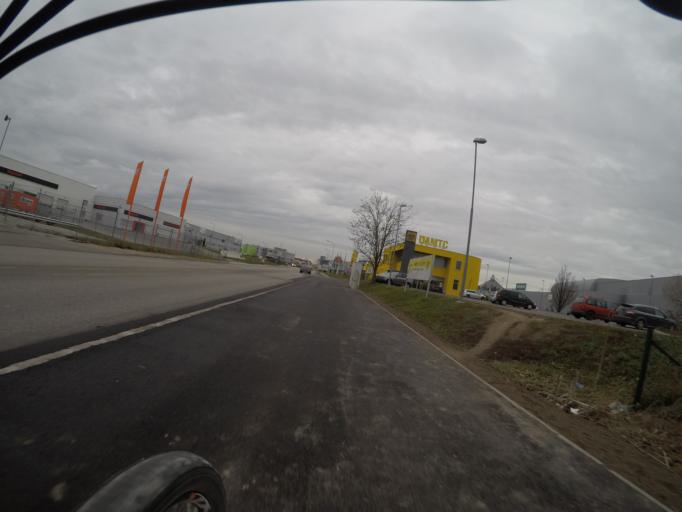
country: AT
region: Lower Austria
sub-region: Politischer Bezirk Modling
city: Wiener Neudorf
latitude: 48.1074
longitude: 16.3105
